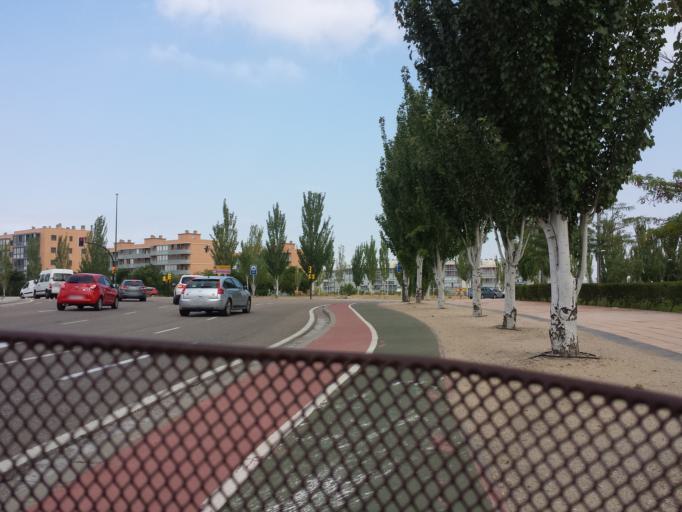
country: ES
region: Aragon
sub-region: Provincia de Zaragoza
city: Montecanal
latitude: 41.6198
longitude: -0.9265
